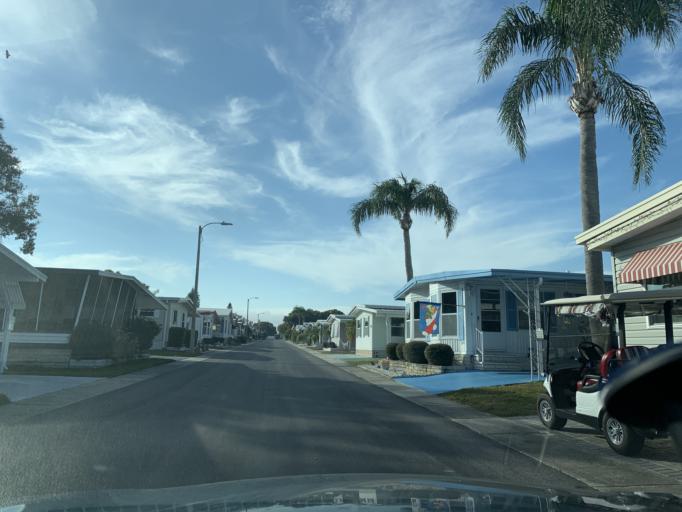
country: US
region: Florida
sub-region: Pinellas County
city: Largo
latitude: 27.8989
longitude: -82.7916
